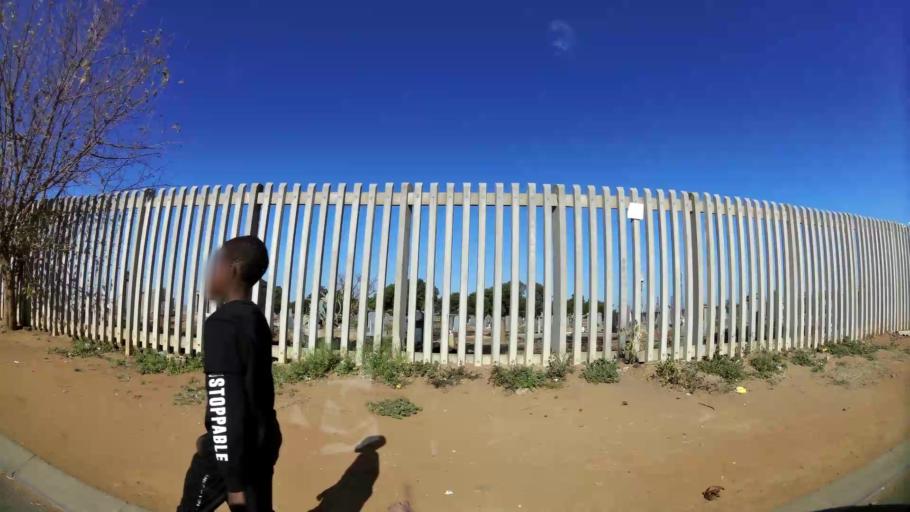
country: ZA
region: Gauteng
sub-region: Ekurhuleni Metropolitan Municipality
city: Tembisa
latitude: -26.0232
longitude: 28.2242
